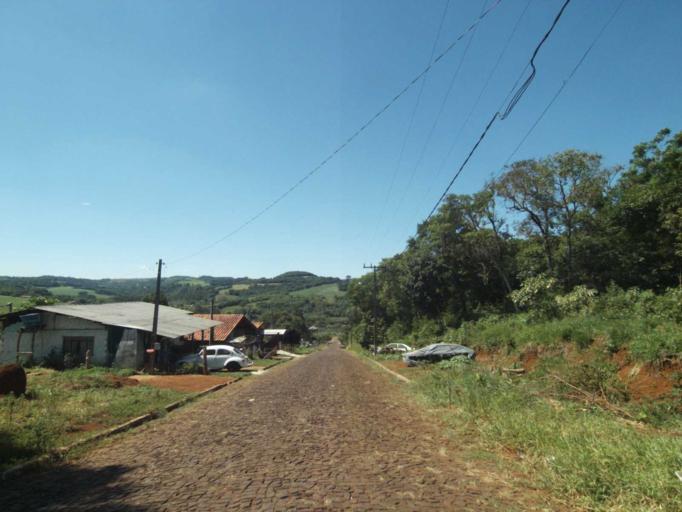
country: BR
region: Parana
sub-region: Laranjeiras Do Sul
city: Laranjeiras do Sul
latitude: -25.3833
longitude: -52.2081
